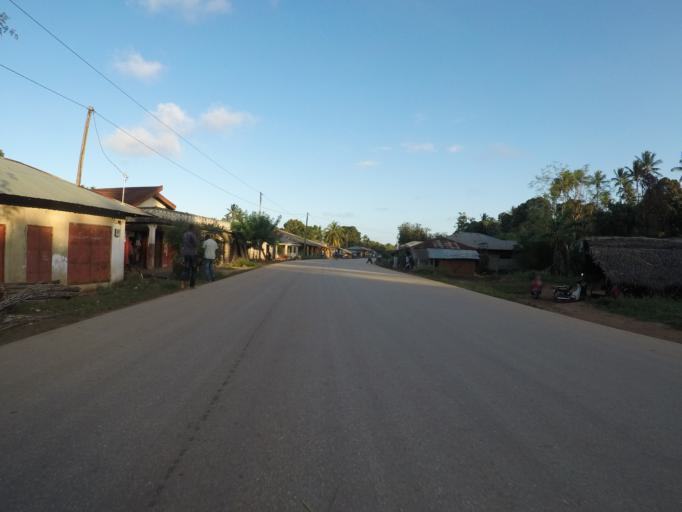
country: TZ
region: Zanzibar North
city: Gamba
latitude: -5.8851
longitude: 39.2861
